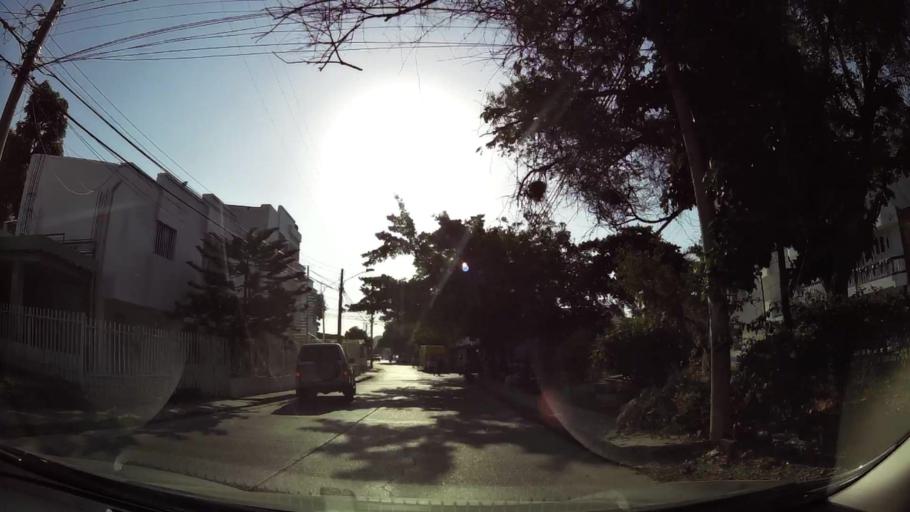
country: CO
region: Bolivar
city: Cartagena
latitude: 10.3999
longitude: -75.4825
